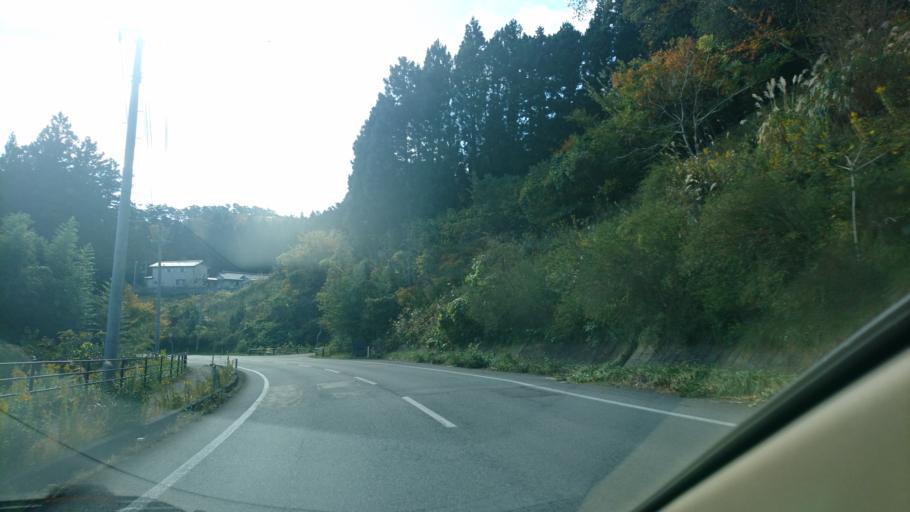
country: JP
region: Iwate
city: Ofunato
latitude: 39.0258
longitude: 141.7049
